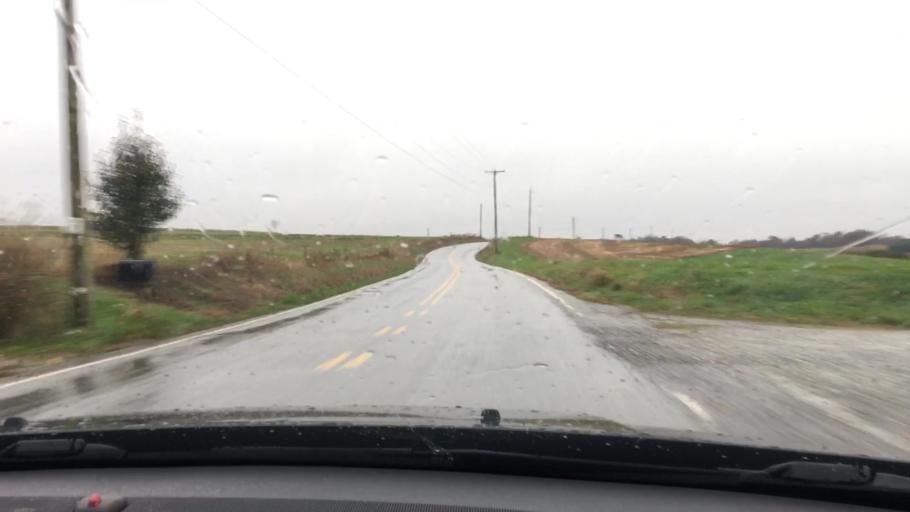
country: US
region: Pennsylvania
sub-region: York County
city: Susquehanna Trails
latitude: 39.7773
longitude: -76.4541
